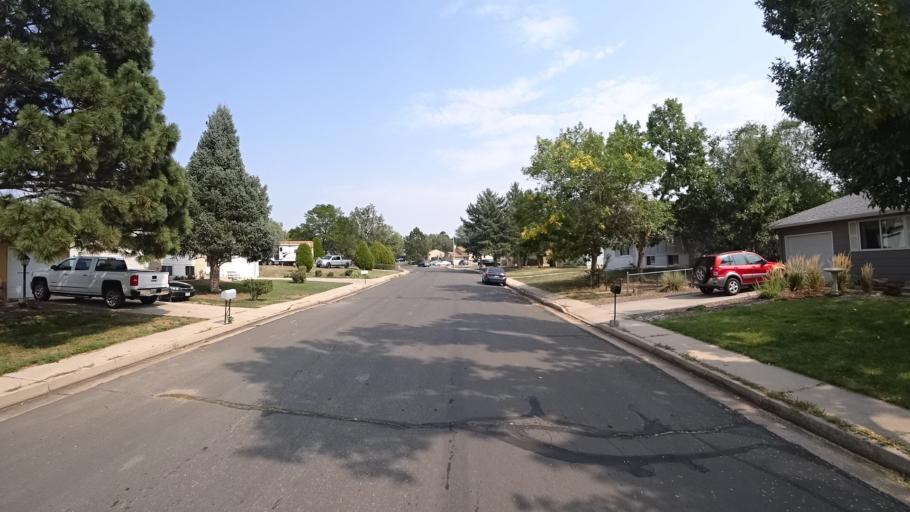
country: US
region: Colorado
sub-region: El Paso County
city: Stratmoor
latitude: 38.8294
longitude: -104.7534
